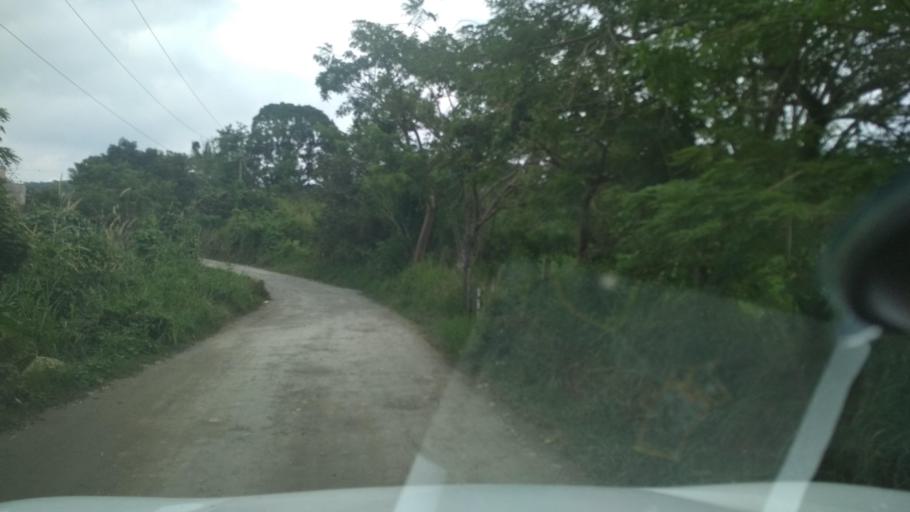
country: MX
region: Veracruz
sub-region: Poza Rica de Hidalgo
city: El Mollejon
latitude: 20.5165
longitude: -97.3826
